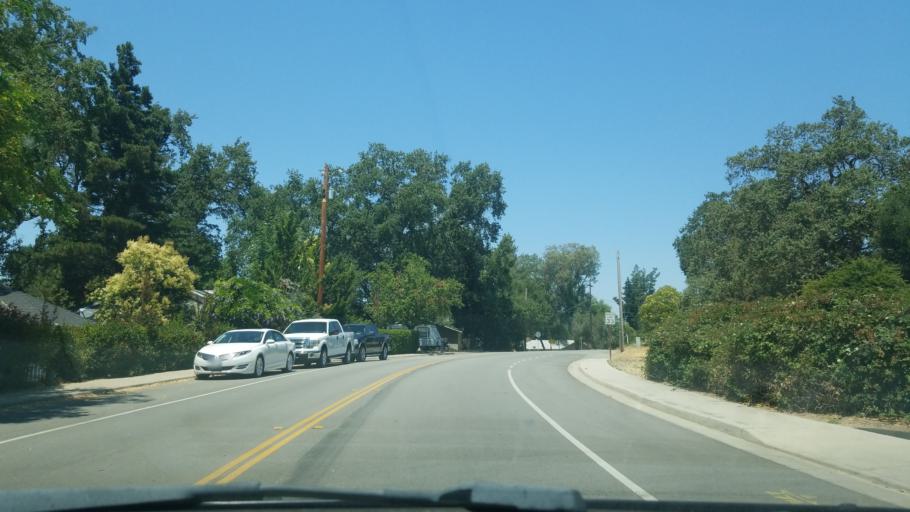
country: US
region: California
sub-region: San Luis Obispo County
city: Atascadero
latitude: 35.4939
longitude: -120.6649
